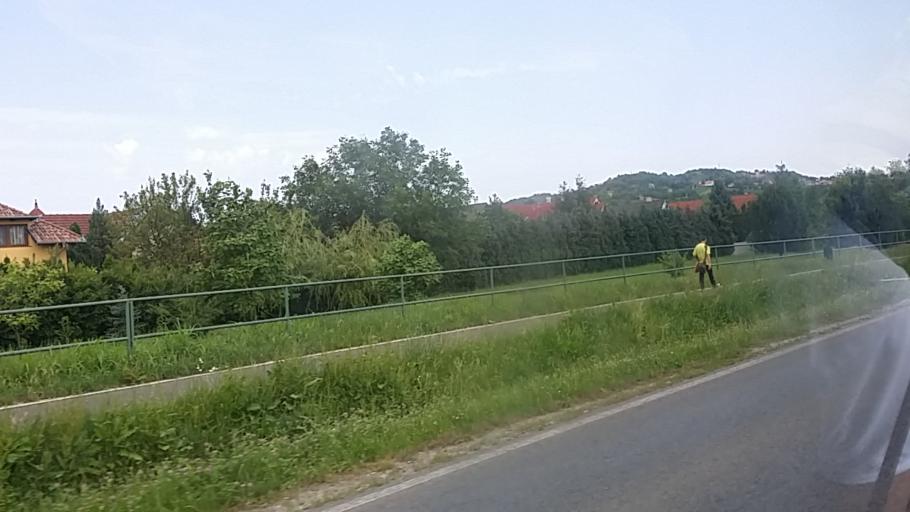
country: HU
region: Tolna
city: Szekszard
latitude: 46.3233
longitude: 18.6978
